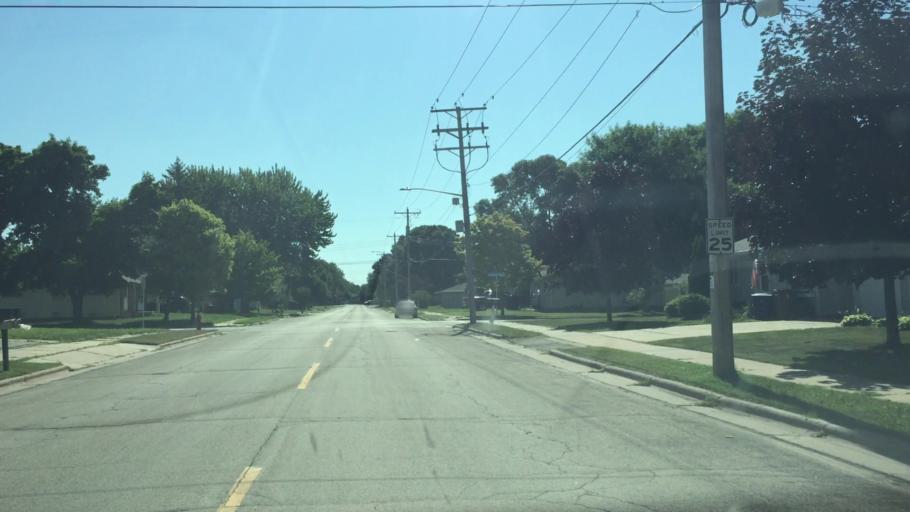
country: US
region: Wisconsin
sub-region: Winnebago County
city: Menasha
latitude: 44.2187
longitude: -88.4177
